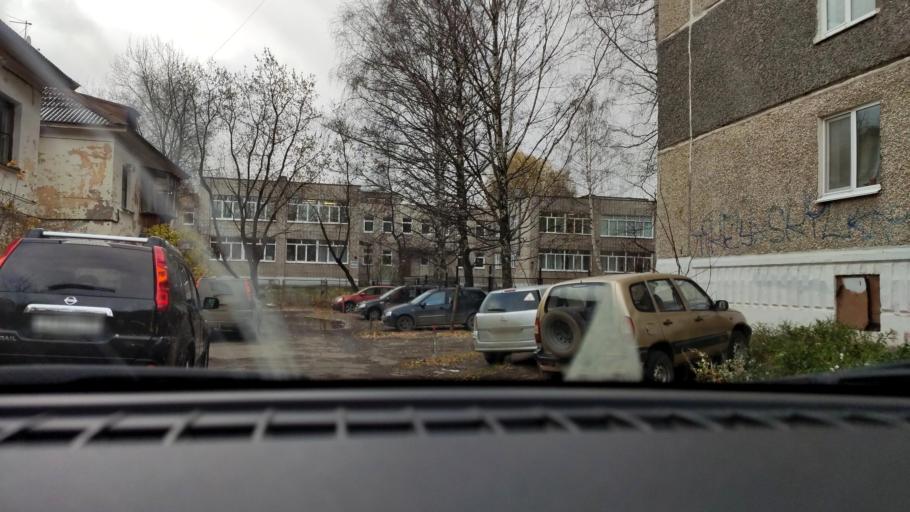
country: RU
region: Perm
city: Perm
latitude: 58.0033
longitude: 56.2744
